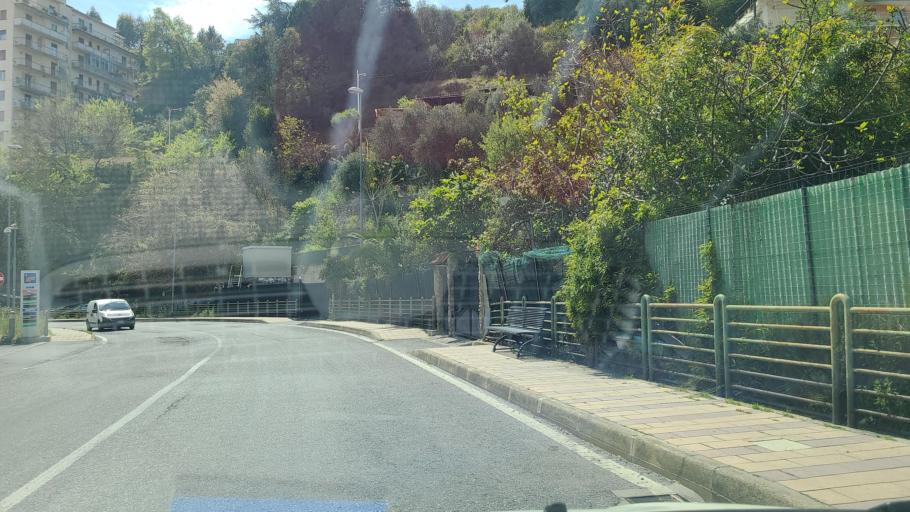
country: IT
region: Liguria
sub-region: Provincia di Imperia
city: San Remo
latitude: 43.8225
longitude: 7.7667
